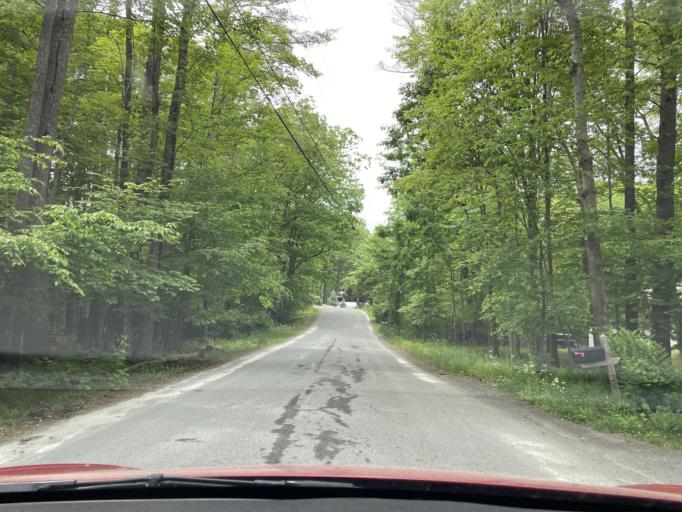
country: US
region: New York
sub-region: Ulster County
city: Zena
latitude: 42.0106
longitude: -74.0778
